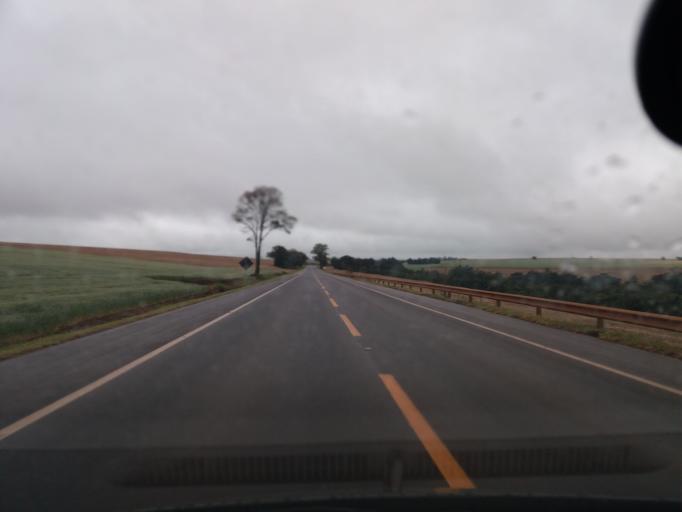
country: BR
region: Parana
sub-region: Campo Mourao
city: Campo Mourao
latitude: -24.3295
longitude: -52.6550
